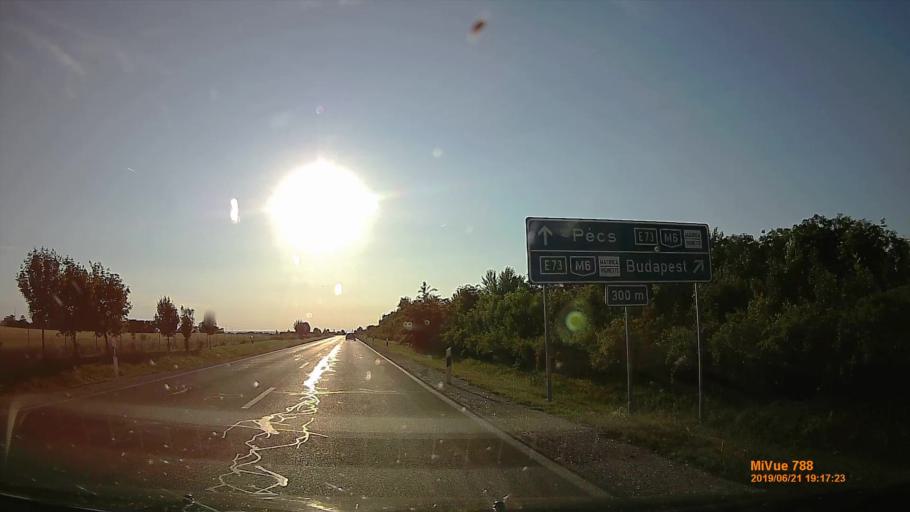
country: HU
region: Fejer
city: Rackeresztur
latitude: 47.3028
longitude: 18.8754
